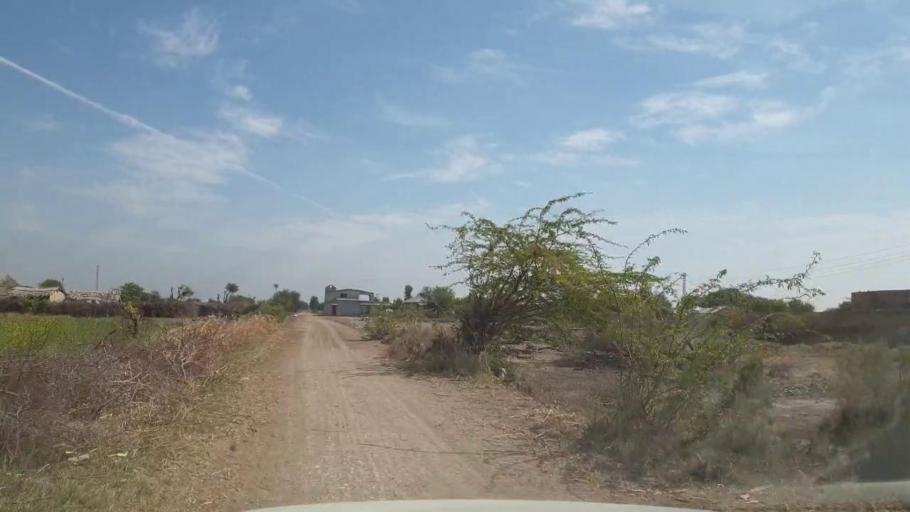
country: PK
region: Sindh
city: Mirpur Khas
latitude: 25.6268
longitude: 69.1969
